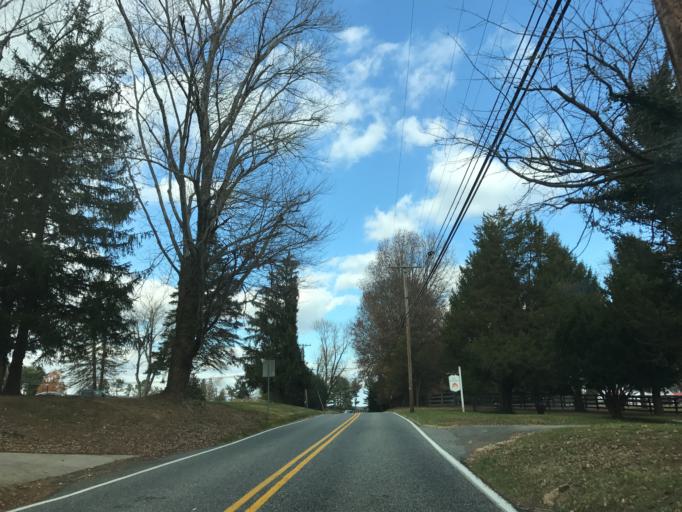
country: US
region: Maryland
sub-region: Harford County
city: Pleasant Hills
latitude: 39.5066
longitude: -76.3730
